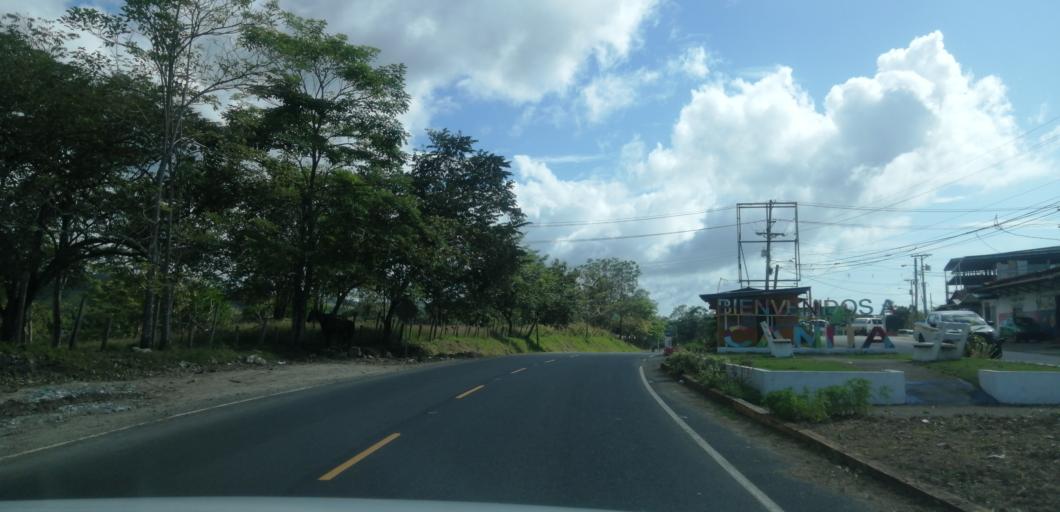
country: PA
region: Panama
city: Canita
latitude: 9.2214
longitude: -78.8913
